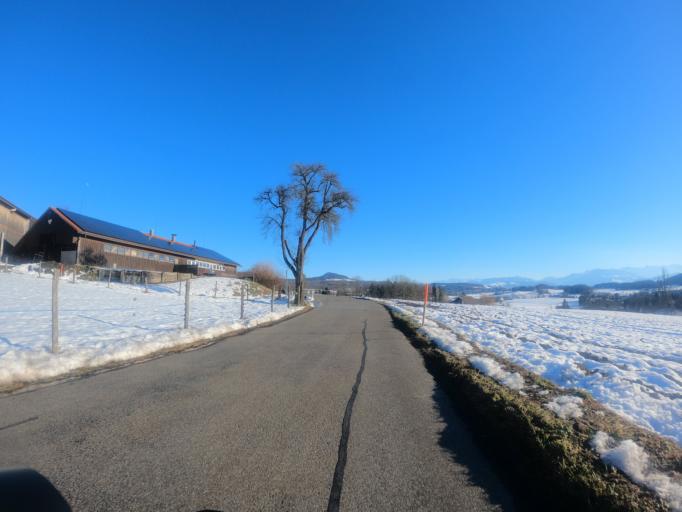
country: CH
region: Zurich
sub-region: Bezirk Affoltern
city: Hedingen
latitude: 47.2978
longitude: 8.4311
